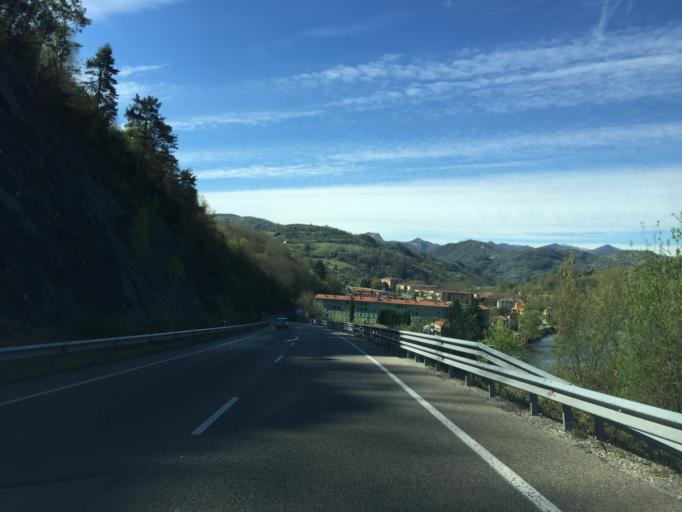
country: ES
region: Asturias
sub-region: Province of Asturias
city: Castandiello
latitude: 43.3574
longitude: -5.9597
